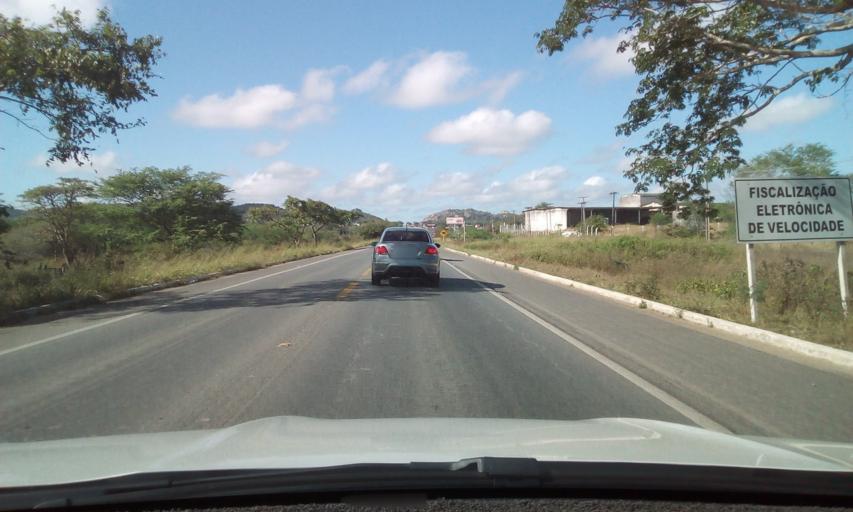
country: BR
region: Paraiba
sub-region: Campina Grande
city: Campina Grande
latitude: -7.3227
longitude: -35.8961
